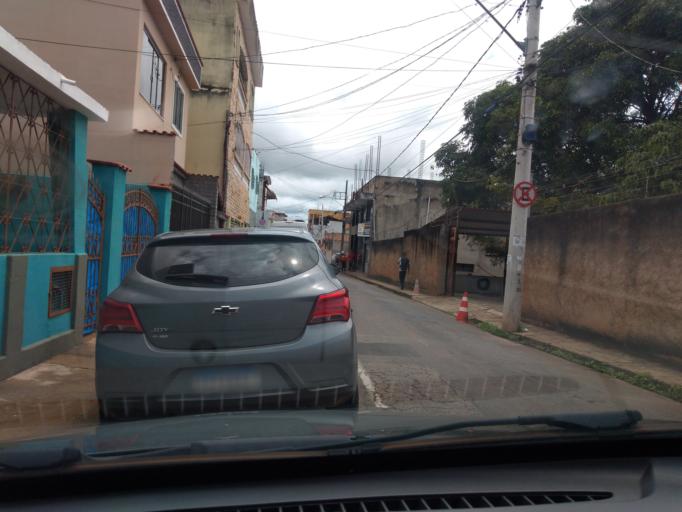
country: BR
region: Minas Gerais
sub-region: Tres Coracoes
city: Tres Coracoes
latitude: -21.6904
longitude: -45.2535
